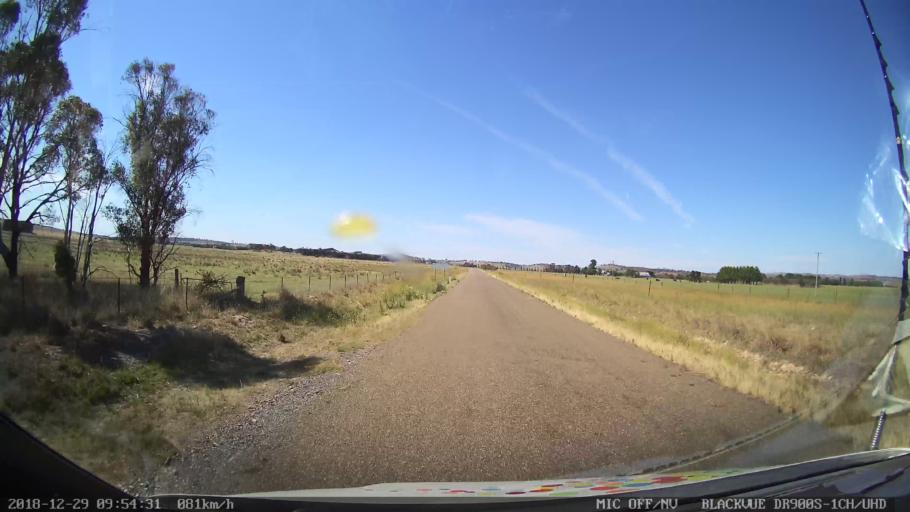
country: AU
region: New South Wales
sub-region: Goulburn Mulwaree
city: Goulburn
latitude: -34.7641
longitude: 149.4669
